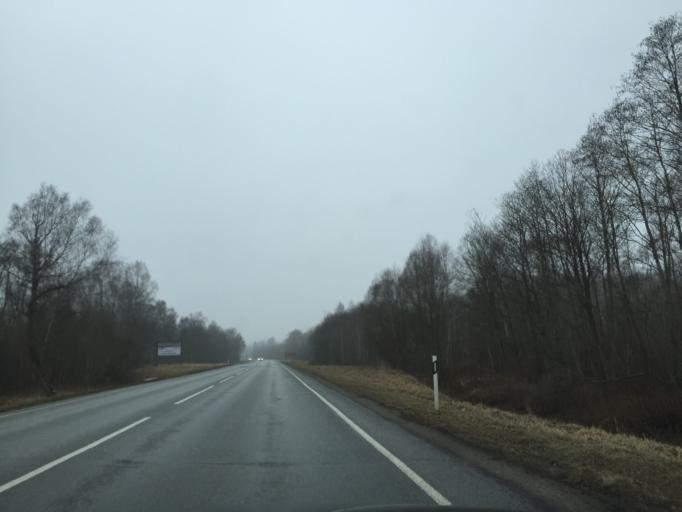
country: EE
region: Laeaene
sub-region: Lihula vald
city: Lihula
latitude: 58.6162
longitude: 23.6061
